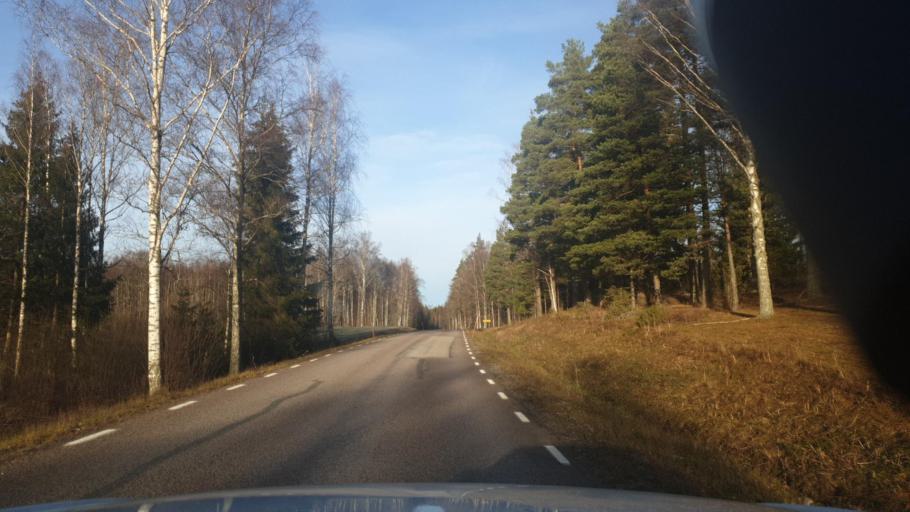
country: SE
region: Vaermland
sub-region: Grums Kommun
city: Slottsbron
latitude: 59.4810
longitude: 12.8837
